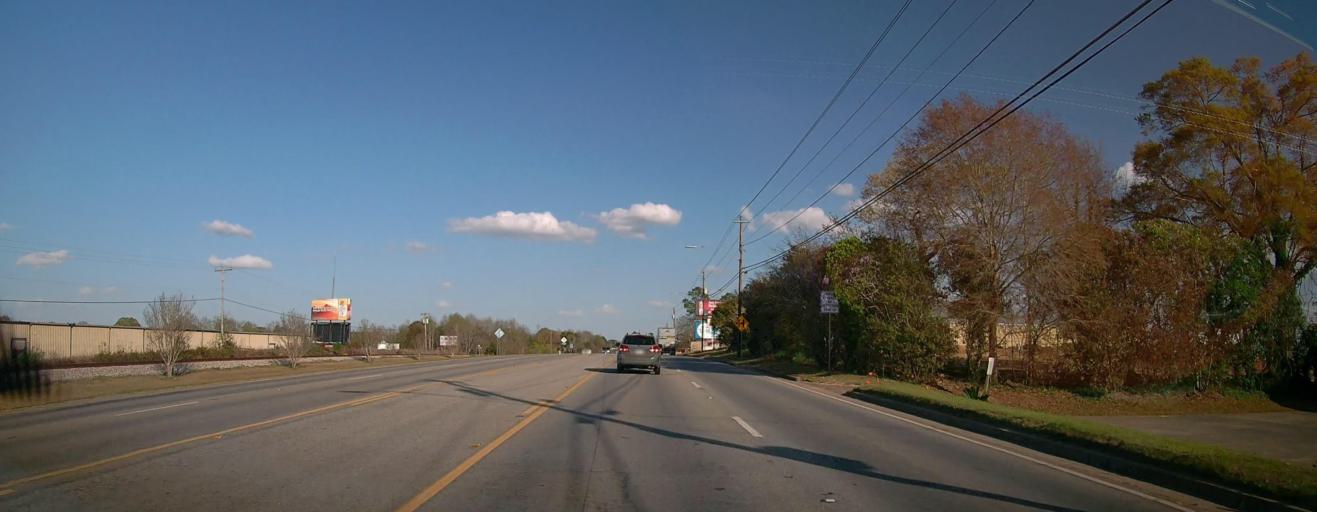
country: US
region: Georgia
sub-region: Toombs County
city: Lyons
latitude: 32.2031
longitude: -82.3502
